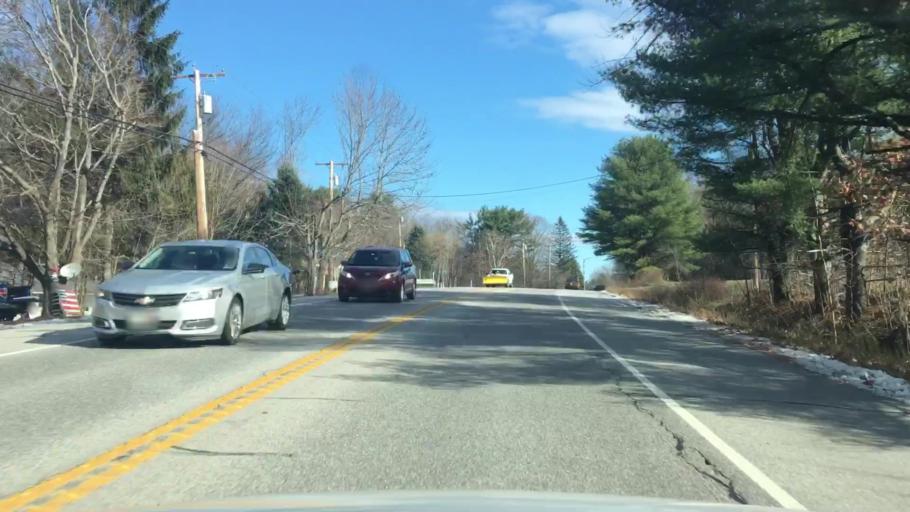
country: US
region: Maine
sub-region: Kennebec County
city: Manchester
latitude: 44.3240
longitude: -69.8851
